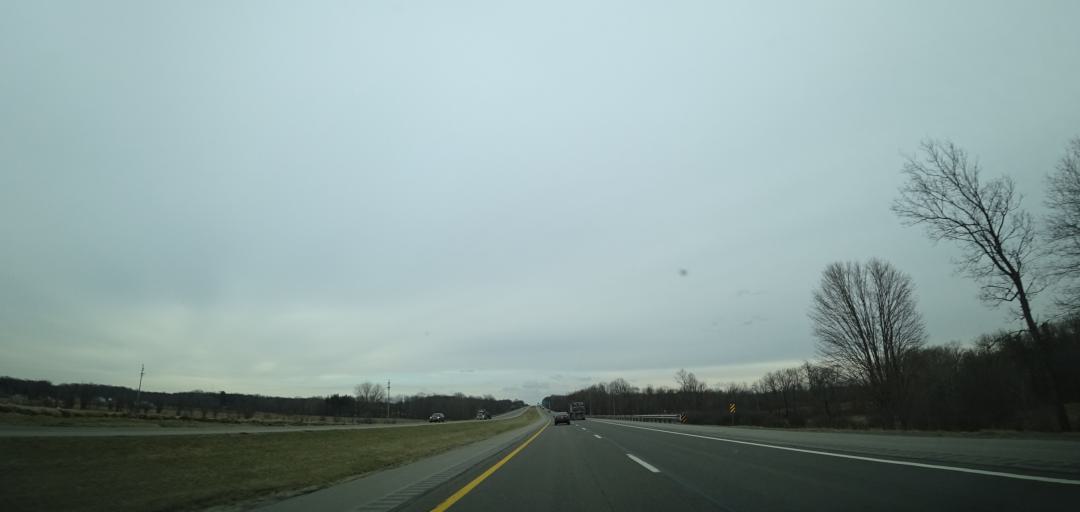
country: US
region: Ohio
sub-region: Mahoning County
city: Boardman
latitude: 40.9803
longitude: -80.6784
